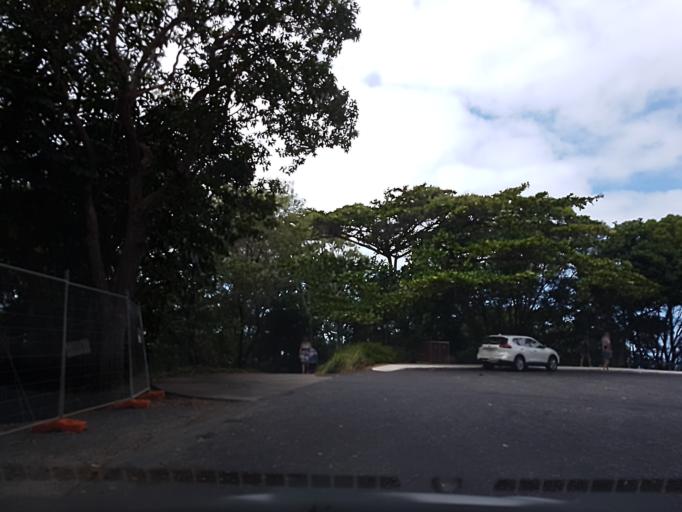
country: AU
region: Queensland
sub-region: Cairns
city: Port Douglas
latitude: -16.4824
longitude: 145.4678
